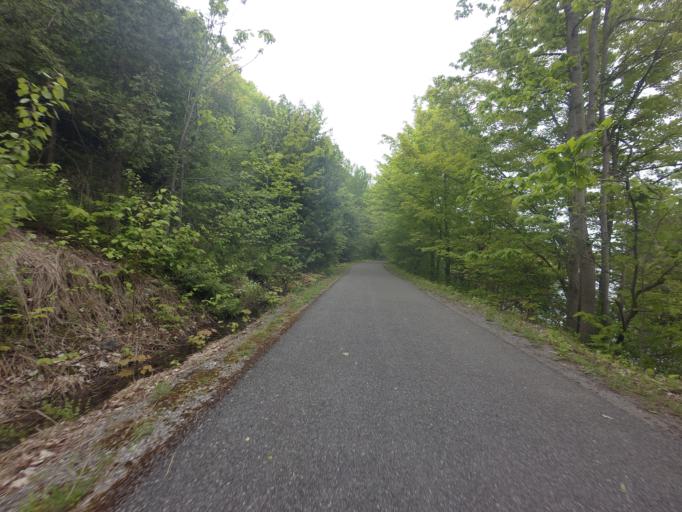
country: US
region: New York
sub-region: Jefferson County
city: Black River
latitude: 43.9914
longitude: -75.8237
